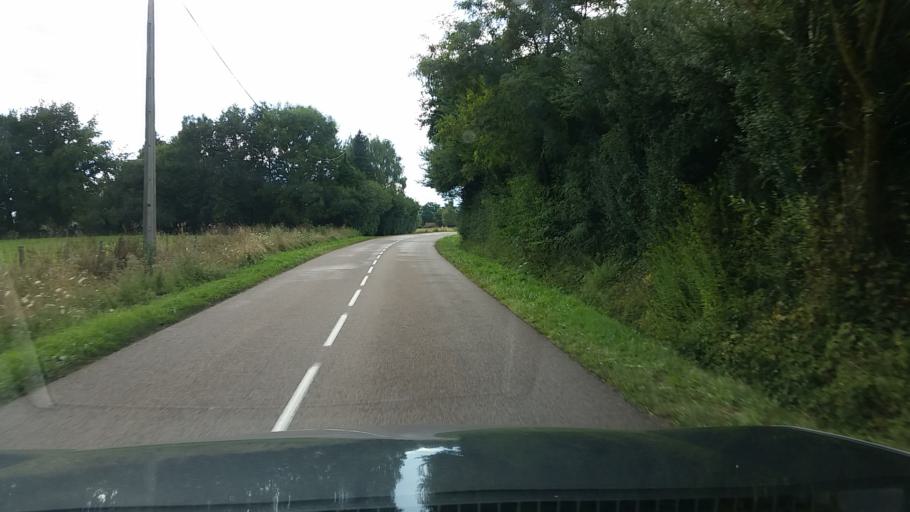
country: FR
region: Bourgogne
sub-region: Departement de Saone-et-Loire
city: Saint-Germain-du-Bois
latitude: 46.7363
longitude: 5.2571
